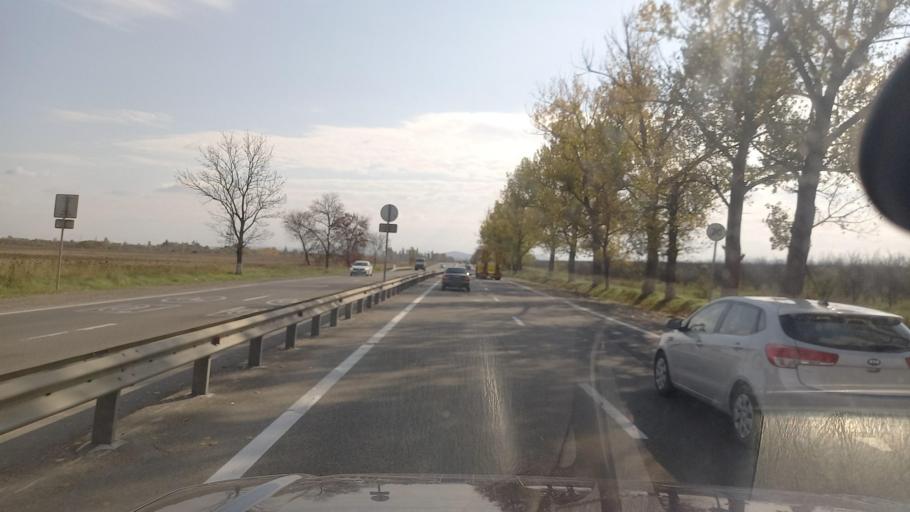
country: RU
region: Krasnodarskiy
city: Akhtyrskiy
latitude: 44.8534
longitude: 38.2652
